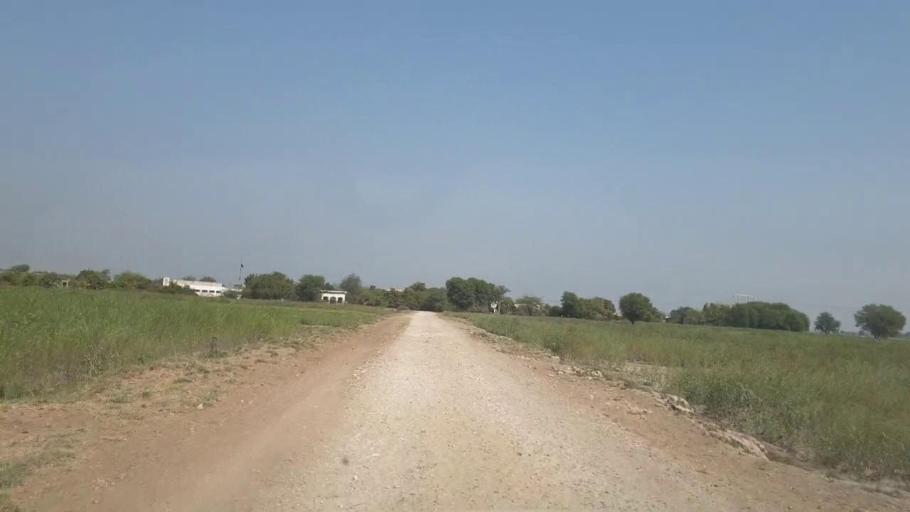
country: PK
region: Sindh
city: Mirpur Khas
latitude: 25.6527
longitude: 69.1051
